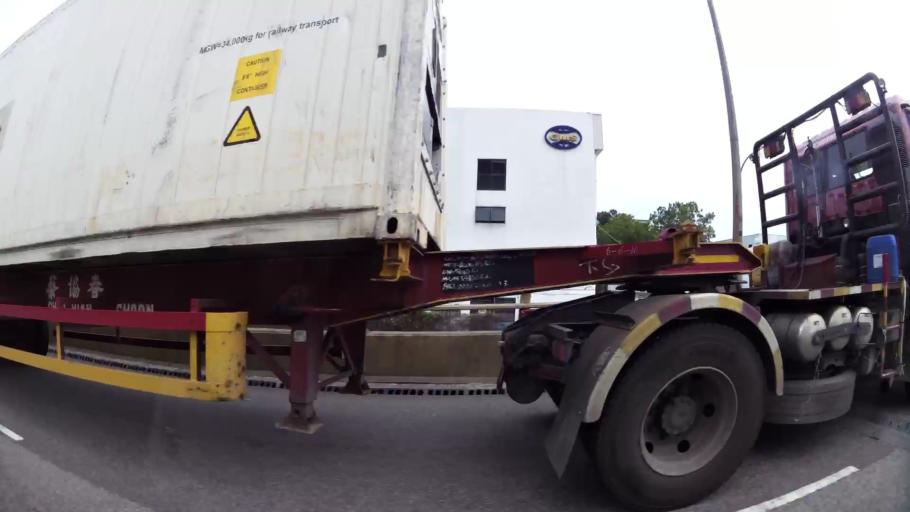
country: SG
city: Singapore
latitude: 1.3117
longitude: 103.7328
